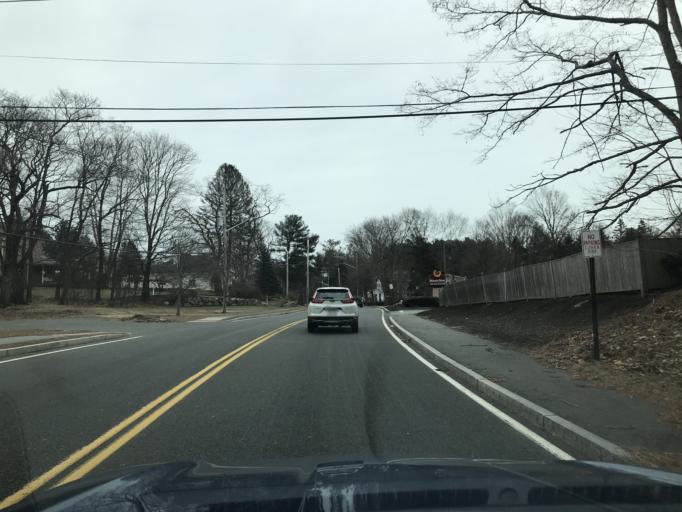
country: US
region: Massachusetts
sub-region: Essex County
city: Lynnfield
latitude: 42.5127
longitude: -71.0246
